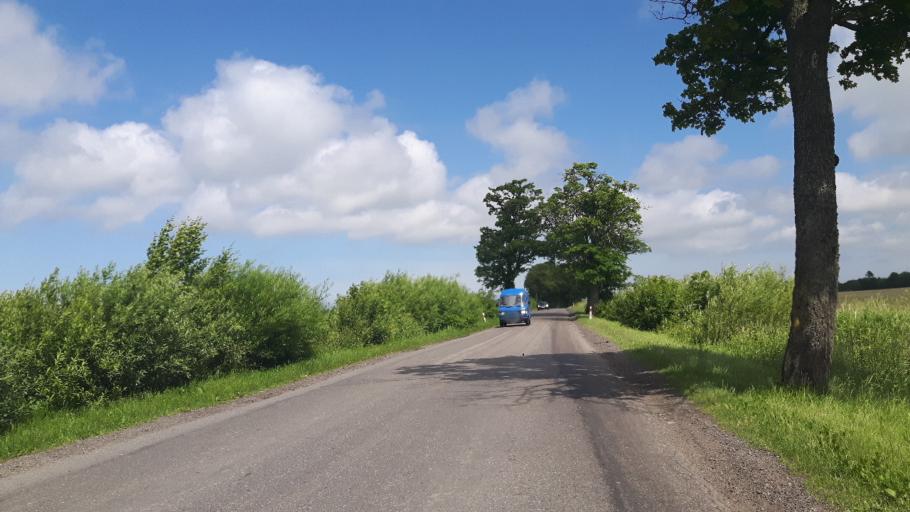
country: PL
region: Pomeranian Voivodeship
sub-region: Powiat slupski
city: Ustka
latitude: 54.5462
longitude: 16.8266
